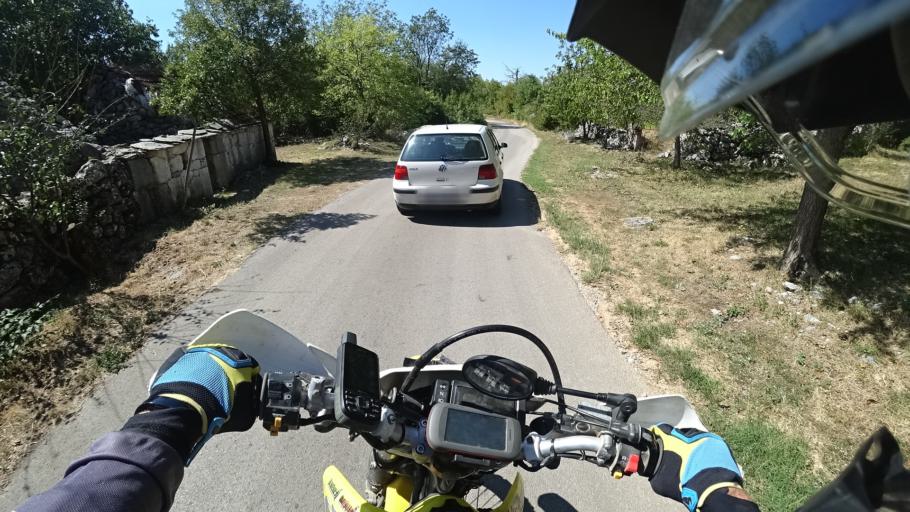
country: HR
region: Splitsko-Dalmatinska
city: Hrvace
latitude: 43.7442
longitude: 16.4404
